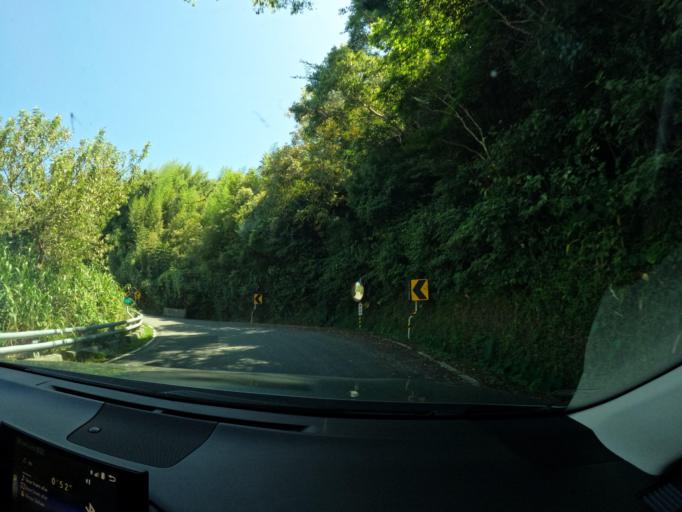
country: TW
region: Taiwan
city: Yujing
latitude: 23.2836
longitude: 120.8410
